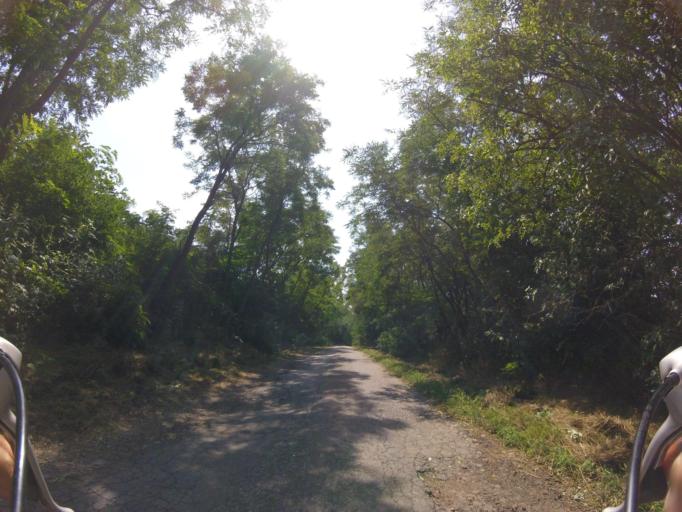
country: SK
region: Nitriansky
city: Sahy
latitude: 48.0460
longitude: 18.8511
